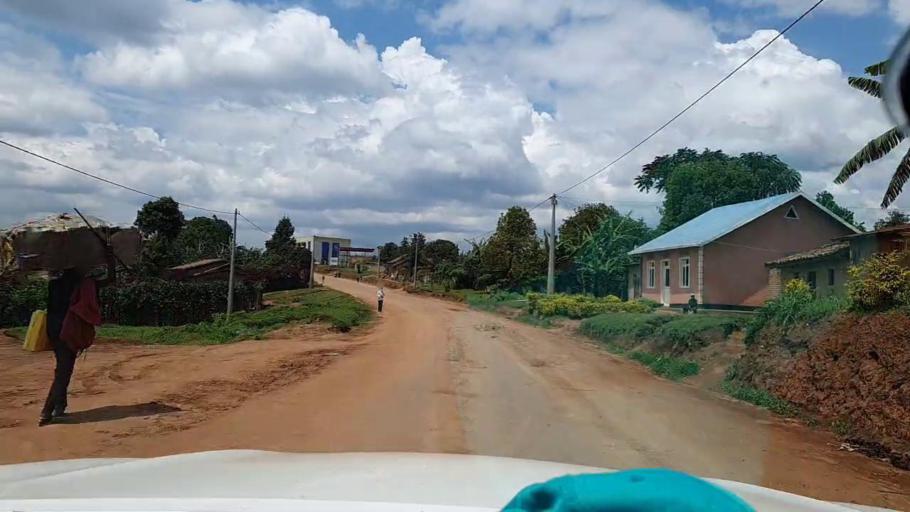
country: RW
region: Southern Province
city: Nzega
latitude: -2.6475
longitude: 29.5632
